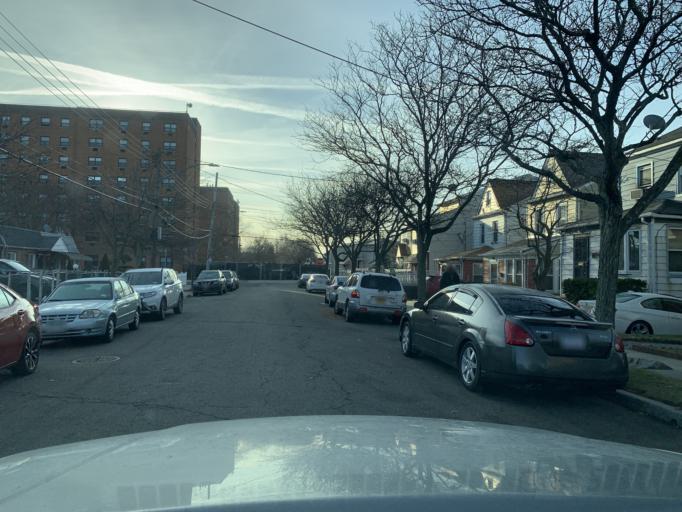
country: US
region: New York
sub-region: Queens County
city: Jamaica
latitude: 40.6918
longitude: -73.7845
